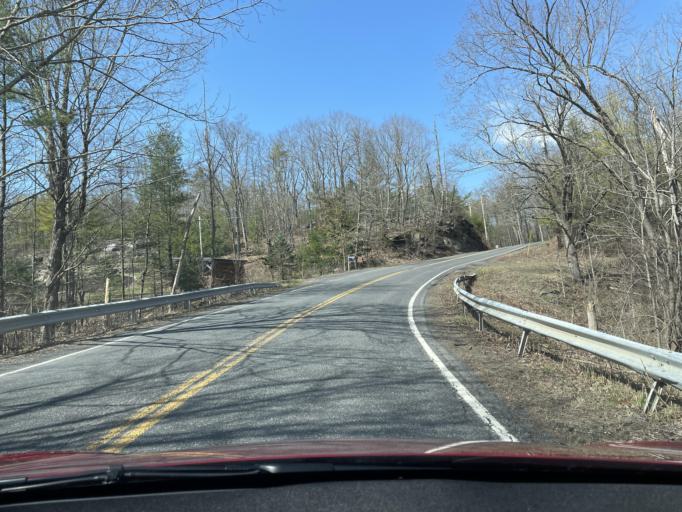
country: US
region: New York
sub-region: Ulster County
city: Manorville
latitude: 42.1051
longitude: -74.0219
